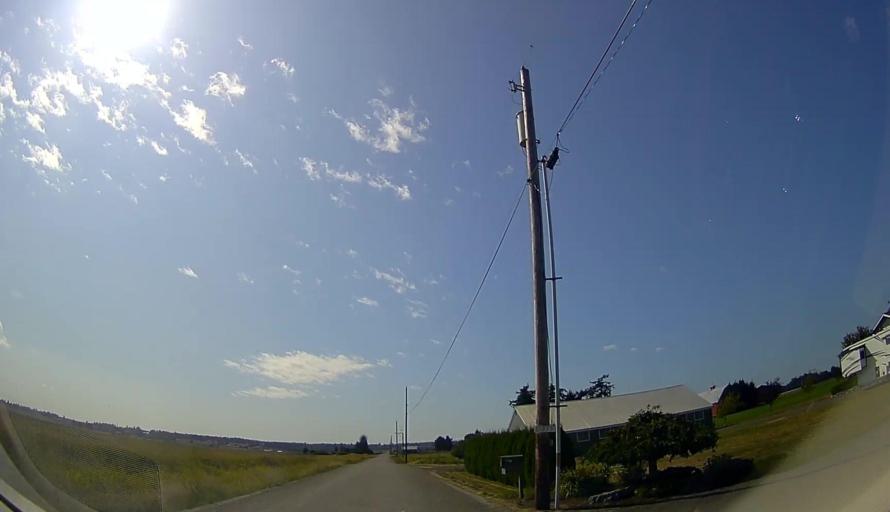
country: US
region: Washington
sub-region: Skagit County
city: Burlington
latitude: 48.4937
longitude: -122.3599
